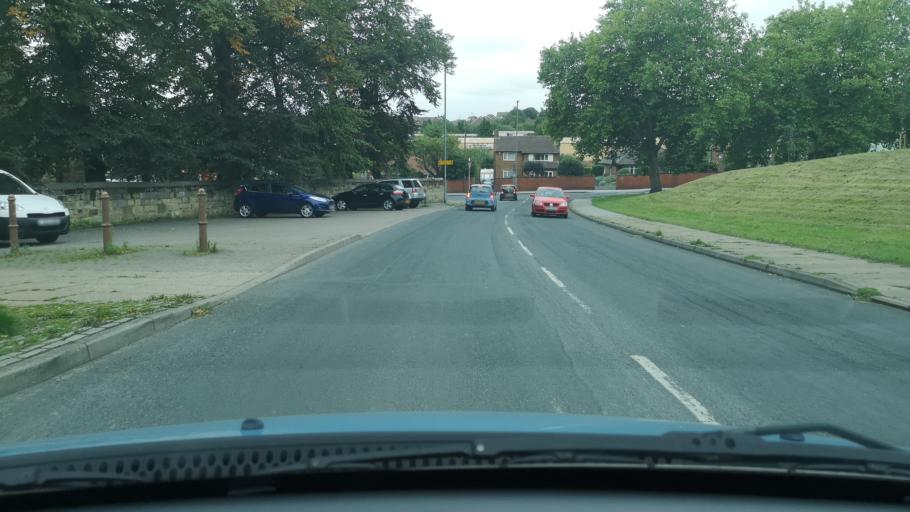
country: GB
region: England
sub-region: City and Borough of Wakefield
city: Pontefract
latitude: 53.6961
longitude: -1.3018
